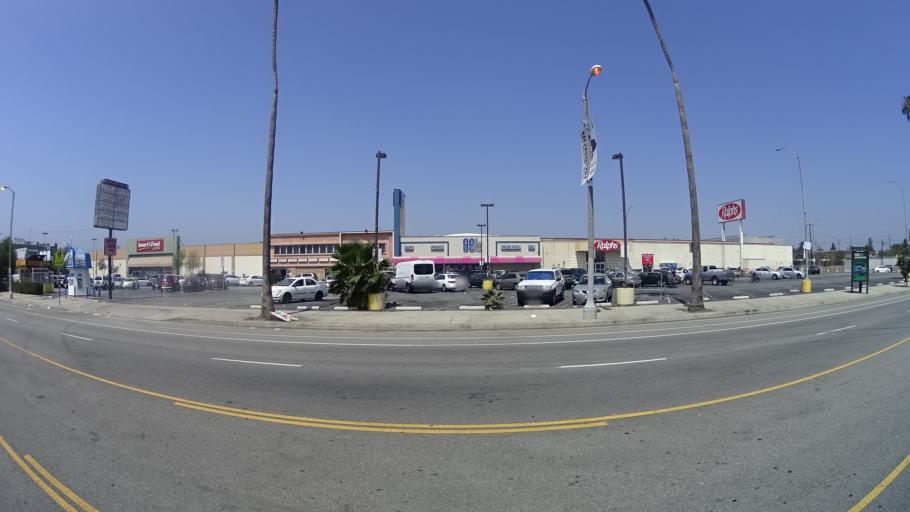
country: US
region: California
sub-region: Los Angeles County
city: North Hollywood
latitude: 34.1915
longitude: -118.3963
